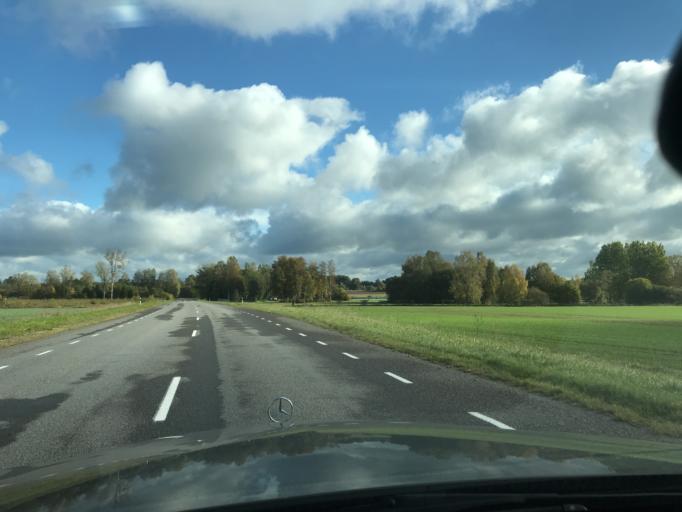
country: EE
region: Valgamaa
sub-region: Torva linn
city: Torva
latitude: 57.9790
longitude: 25.9936
